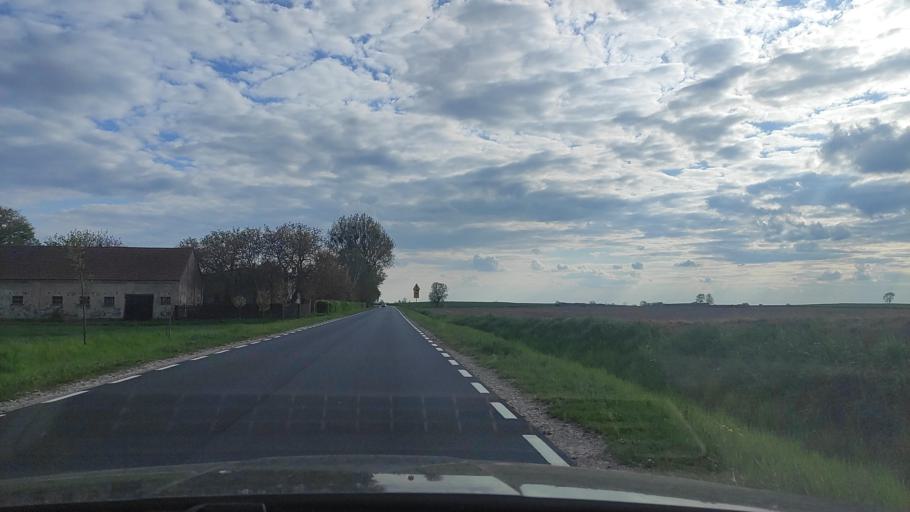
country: PL
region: Greater Poland Voivodeship
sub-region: Powiat poznanski
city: Kostrzyn
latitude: 52.4352
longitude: 17.2364
